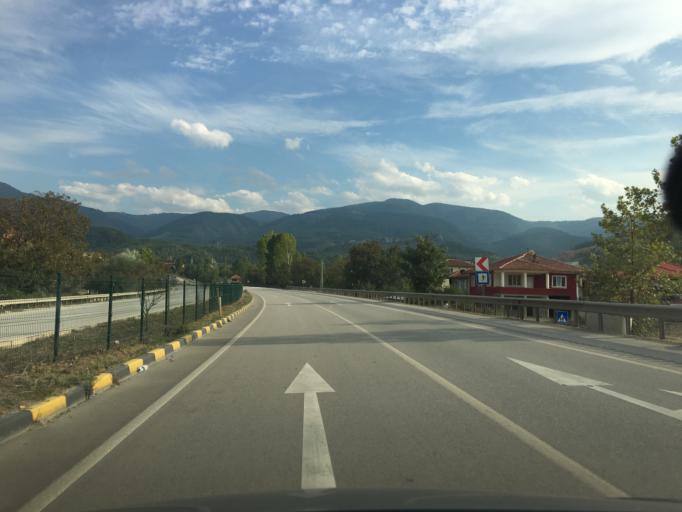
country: TR
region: Karabuk
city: Karabuk
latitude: 41.1015
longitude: 32.6698
